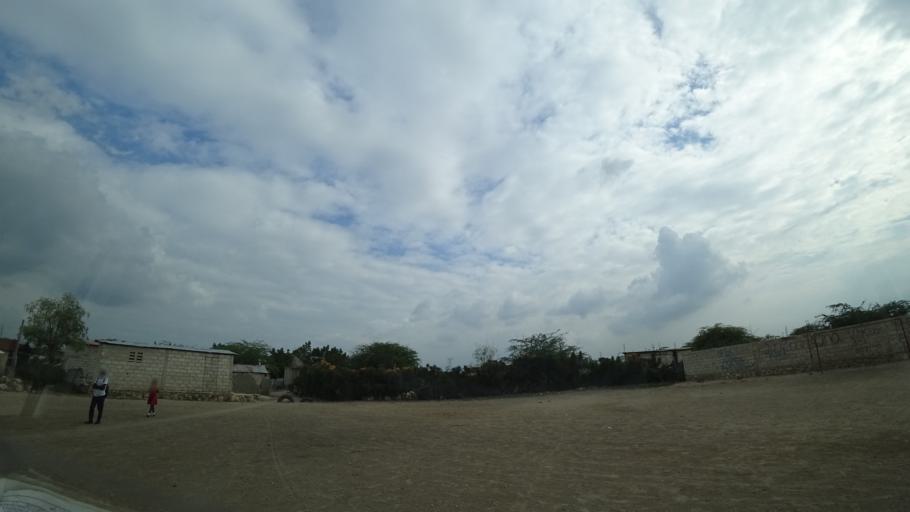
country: HT
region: Ouest
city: Croix des Bouquets
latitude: 18.6569
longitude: -72.2577
